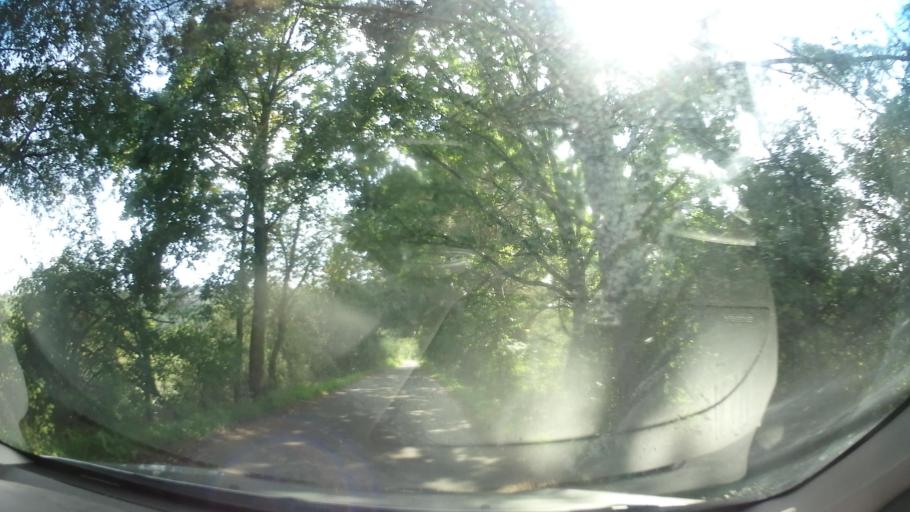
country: CZ
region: Central Bohemia
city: Krasna Hora nad Vltavou
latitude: 49.6928
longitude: 14.3225
